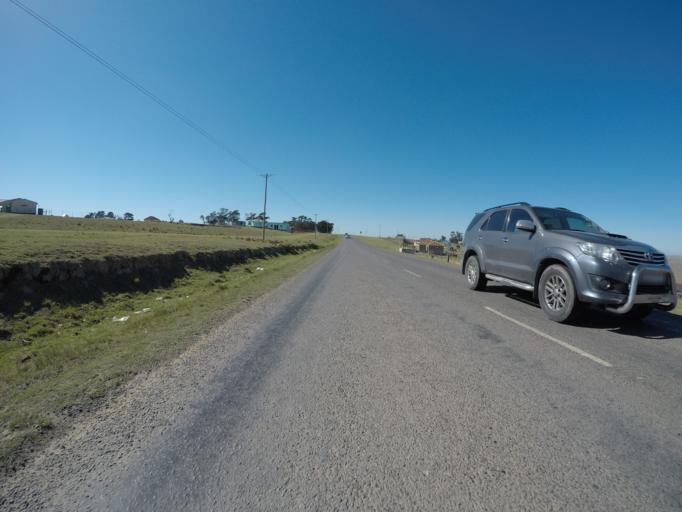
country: ZA
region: Eastern Cape
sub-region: OR Tambo District Municipality
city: Mthatha
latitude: -31.7883
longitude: 28.7435
